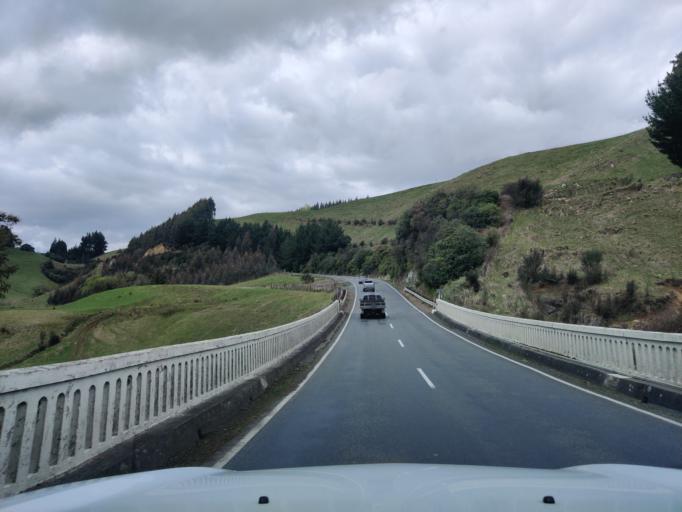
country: NZ
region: Manawatu-Wanganui
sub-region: Ruapehu District
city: Waiouru
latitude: -39.4979
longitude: 175.2900
